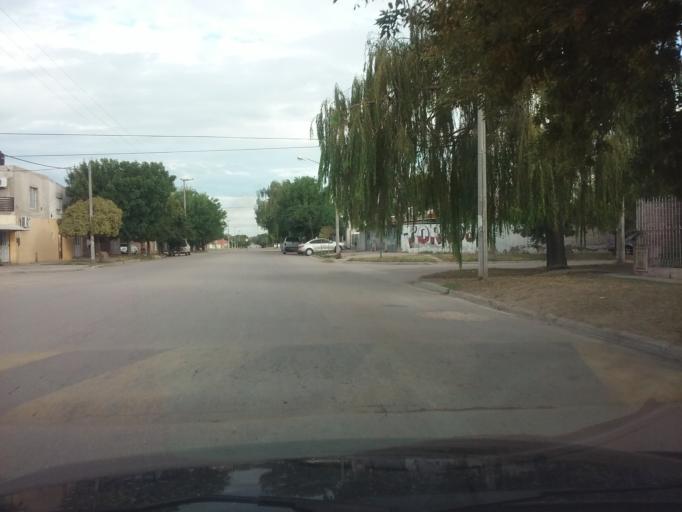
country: AR
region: La Pampa
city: Santa Rosa
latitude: -36.6462
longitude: -64.2942
